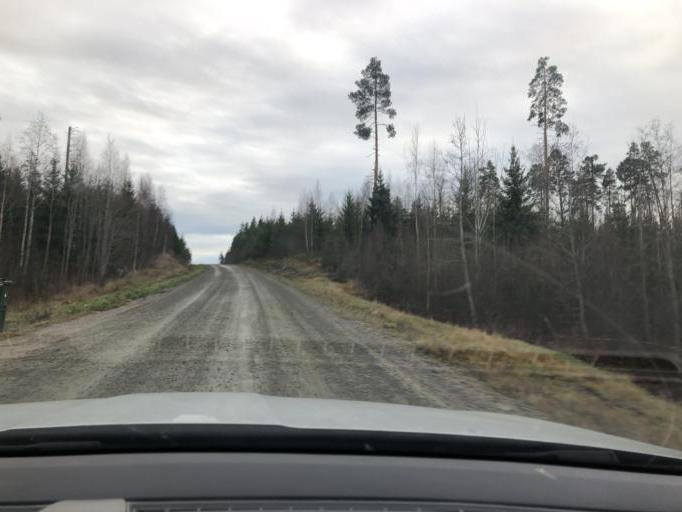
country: SE
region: Gaevleborg
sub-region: Hudiksvalls Kommun
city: Sorforsa
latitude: 61.6502
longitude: 16.9307
